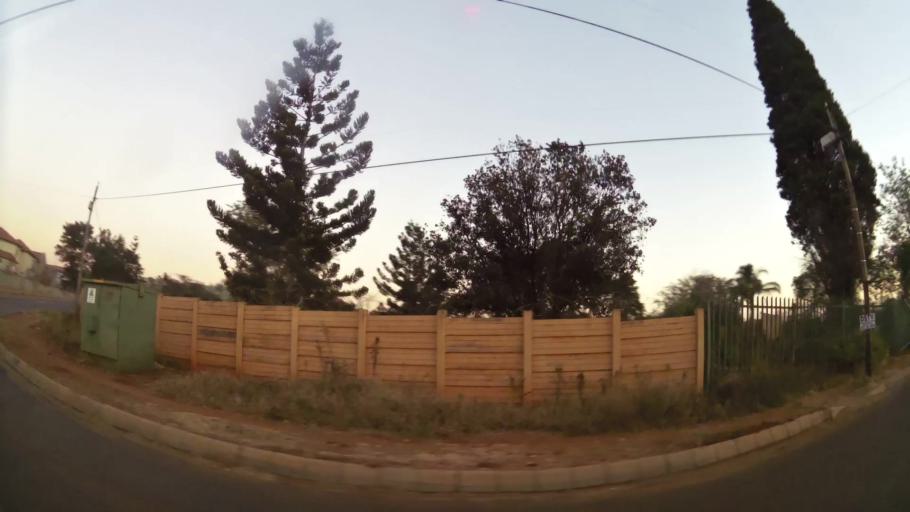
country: ZA
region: Gauteng
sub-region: City of Tshwane Metropolitan Municipality
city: Centurion
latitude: -25.8443
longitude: 28.1262
